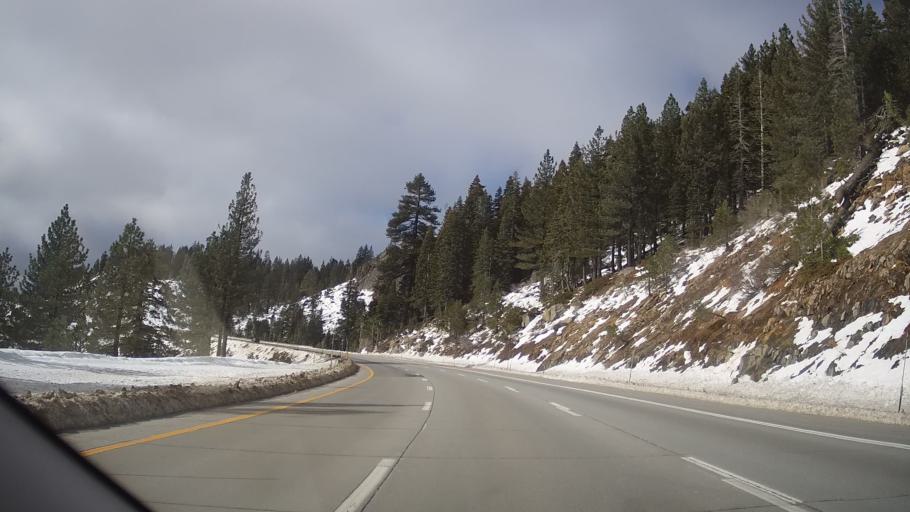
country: US
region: California
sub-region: Nevada County
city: Truckee
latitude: 39.3418
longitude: -120.3123
